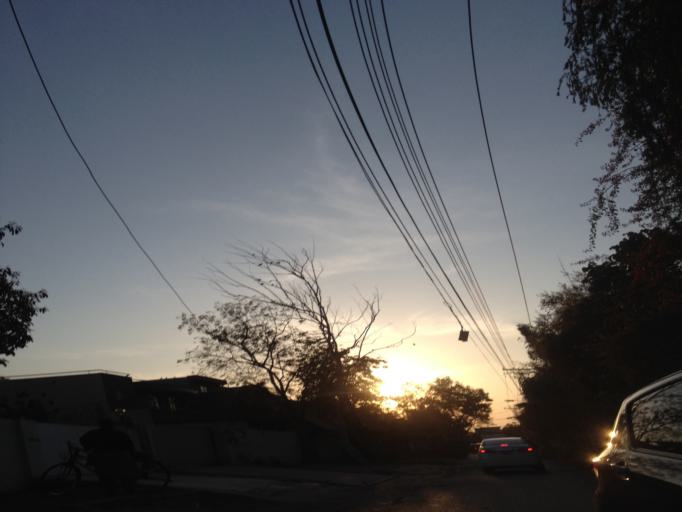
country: PK
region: Punjab
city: Lahore
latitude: 31.4990
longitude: 74.3274
